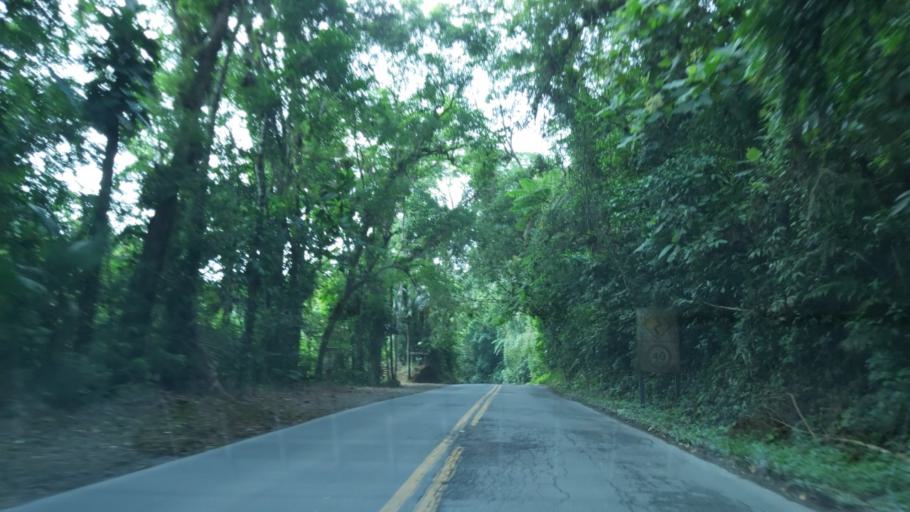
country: BR
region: Sao Paulo
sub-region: Juquia
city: Juquia
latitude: -24.0687
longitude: -47.6008
